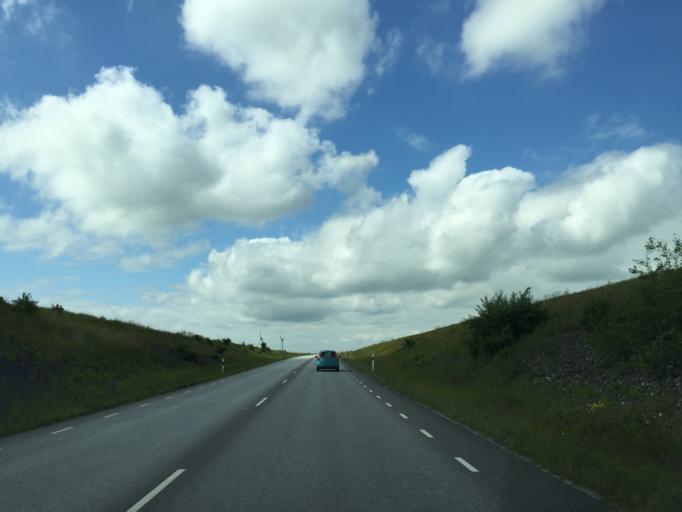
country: SE
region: Skane
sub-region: Staffanstorps Kommun
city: Hjaerup
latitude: 55.6863
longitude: 13.1560
